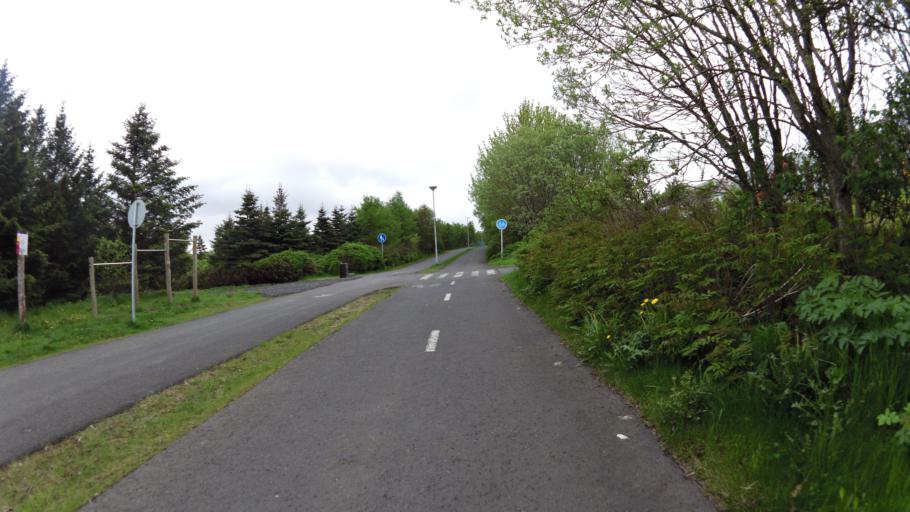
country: IS
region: Capital Region
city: Reykjavik
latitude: 64.1396
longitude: -21.8795
